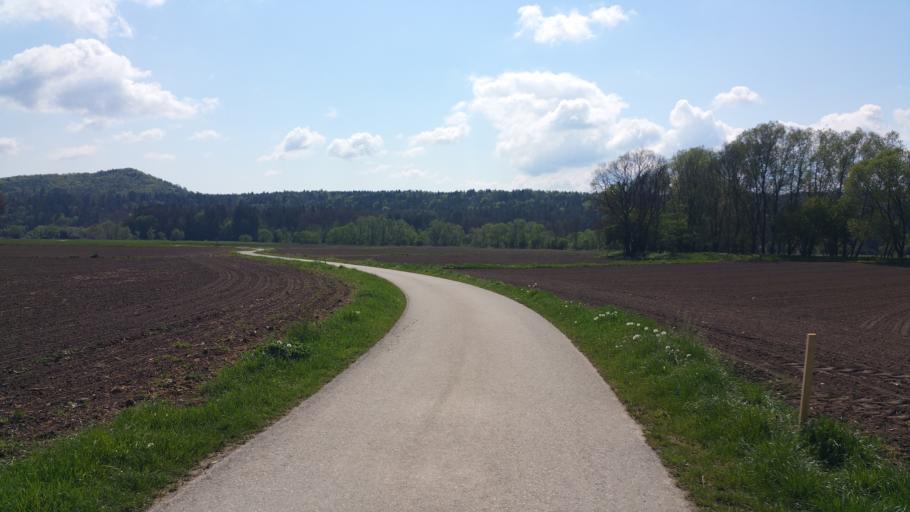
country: AT
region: Styria
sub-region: Politischer Bezirk Leibnitz
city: Gleinstatten
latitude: 46.7560
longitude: 15.3846
